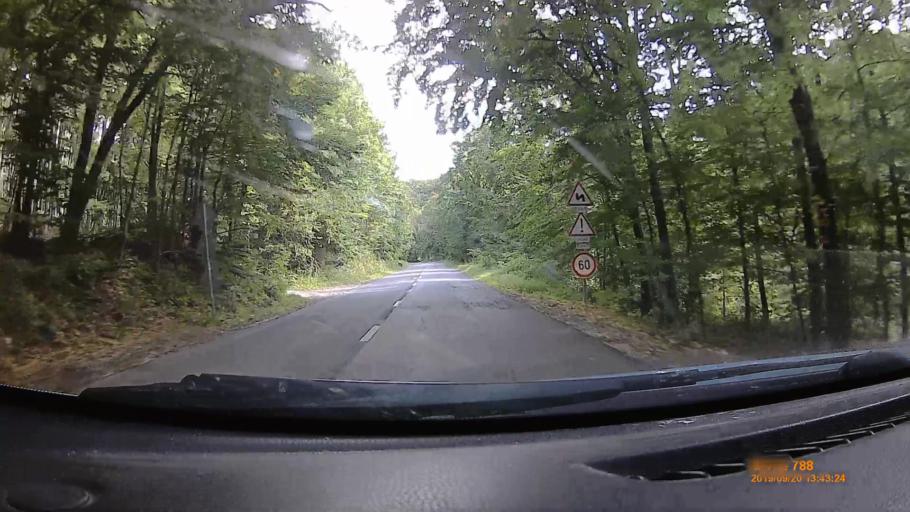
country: HU
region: Borsod-Abauj-Zemplen
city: Saly
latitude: 48.0585
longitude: 20.5536
